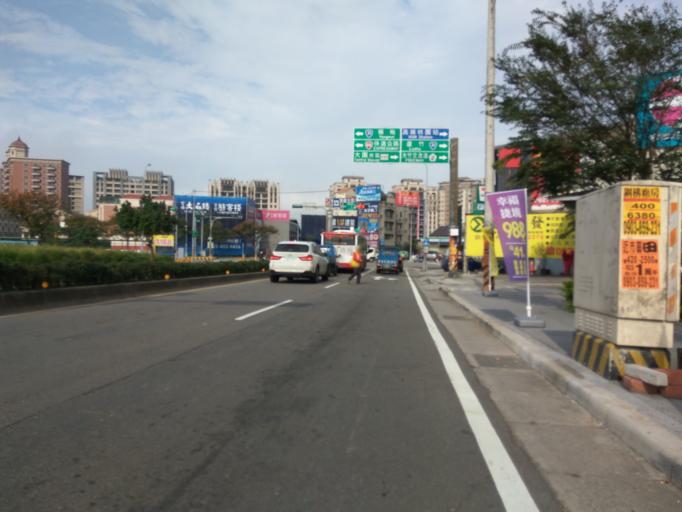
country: TW
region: Taiwan
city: Taoyuan City
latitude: 25.0036
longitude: 121.2142
